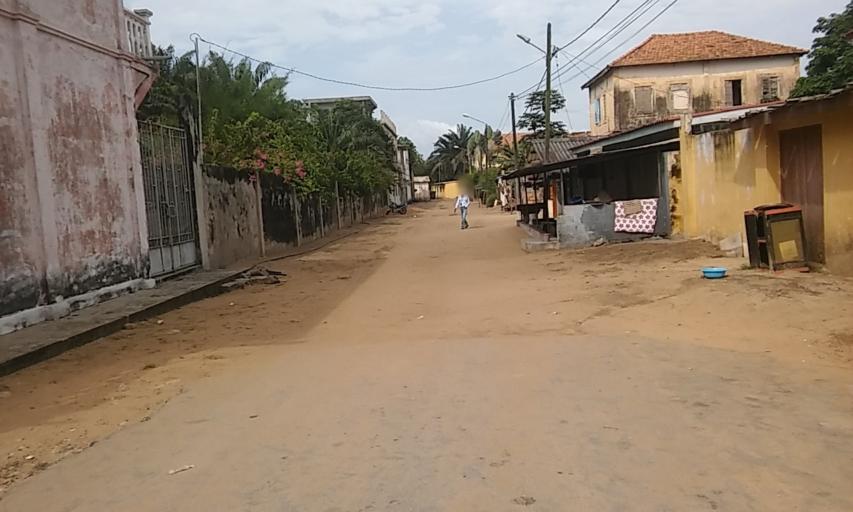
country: CI
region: Sud-Comoe
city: Grand-Bassam
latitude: 5.1949
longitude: -3.7299
